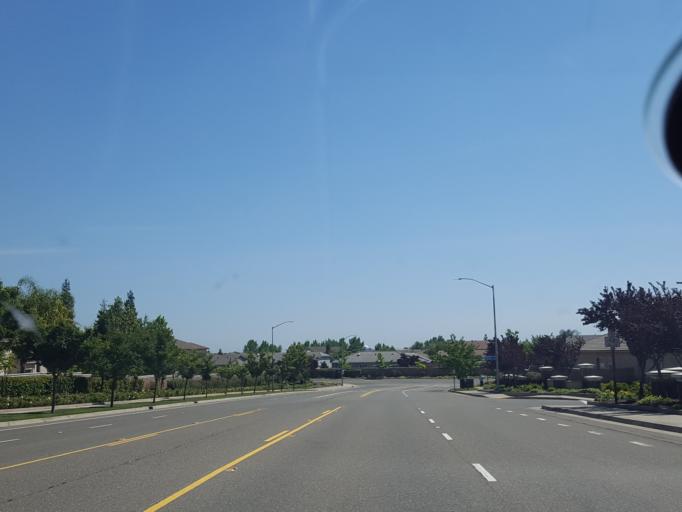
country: US
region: California
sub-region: Sacramento County
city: Rancho Cordova
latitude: 38.5828
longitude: -121.2704
